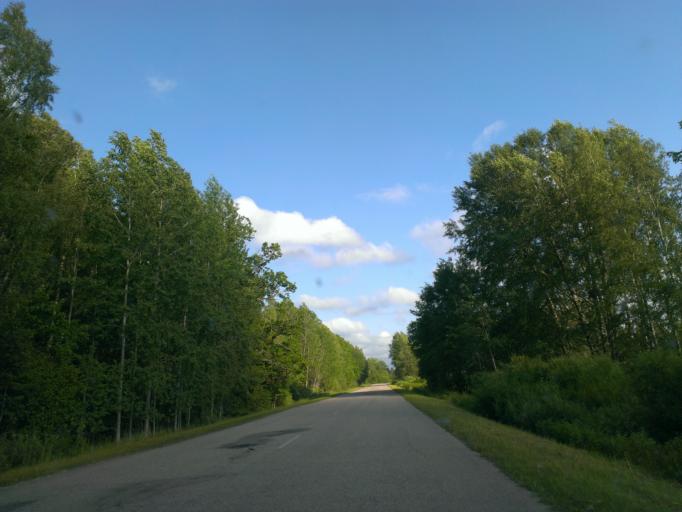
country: LV
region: Aizpute
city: Aizpute
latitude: 56.7912
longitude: 21.5091
